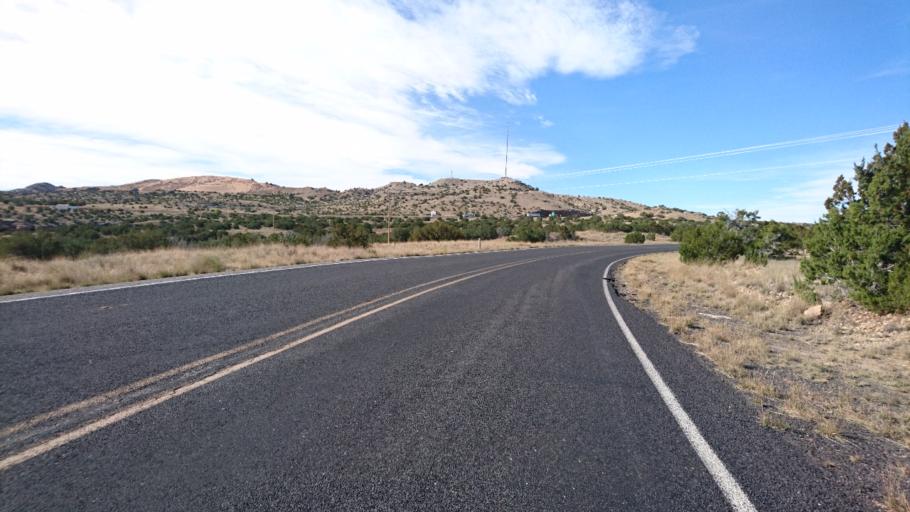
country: US
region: New Mexico
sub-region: Cibola County
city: Laguna
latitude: 35.0427
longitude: -107.3527
